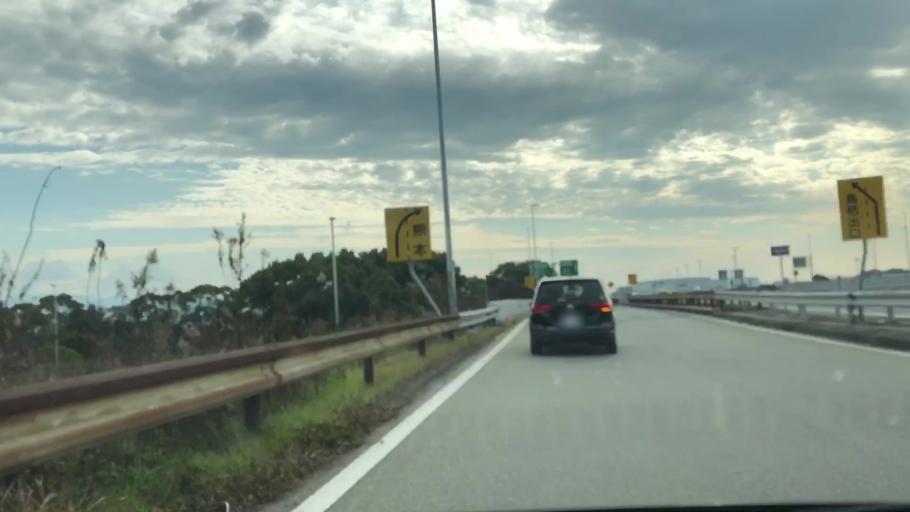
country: JP
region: Saga Prefecture
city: Tosu
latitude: 33.3971
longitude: 130.5387
